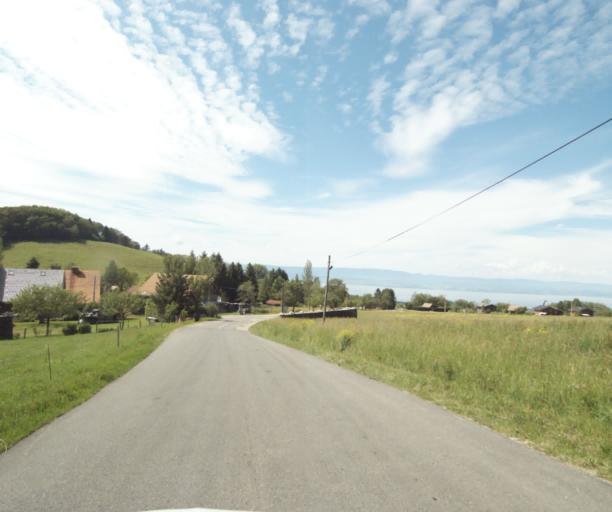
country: FR
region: Rhone-Alpes
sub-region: Departement de la Haute-Savoie
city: Perrignier
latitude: 46.2943
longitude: 6.4749
